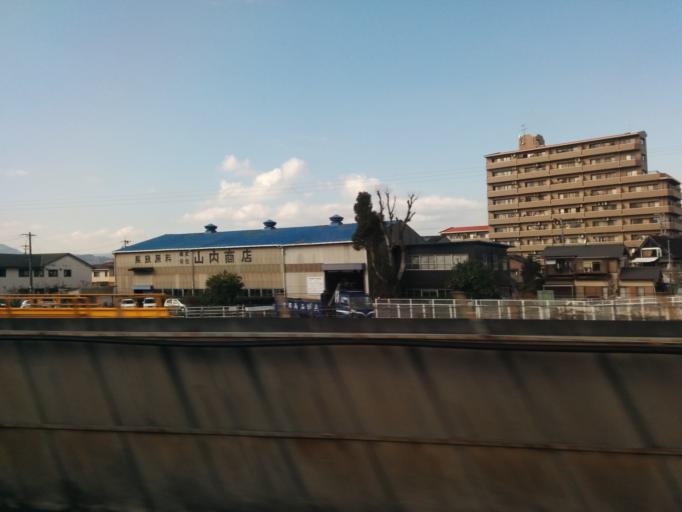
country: JP
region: Shizuoka
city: Shizuoka-shi
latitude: 34.9918
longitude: 138.4240
